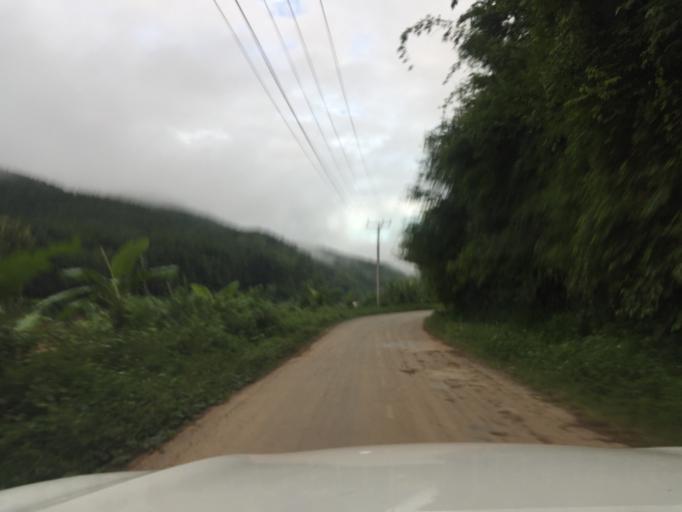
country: LA
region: Phongsali
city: Khoa
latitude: 21.0787
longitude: 102.3756
